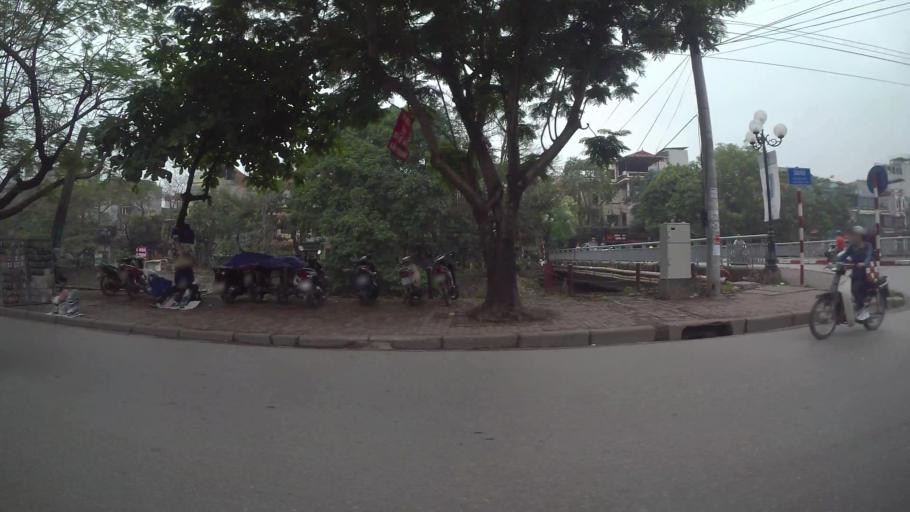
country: VN
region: Ha Noi
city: Hai BaTrung
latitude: 20.9880
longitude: 105.8634
